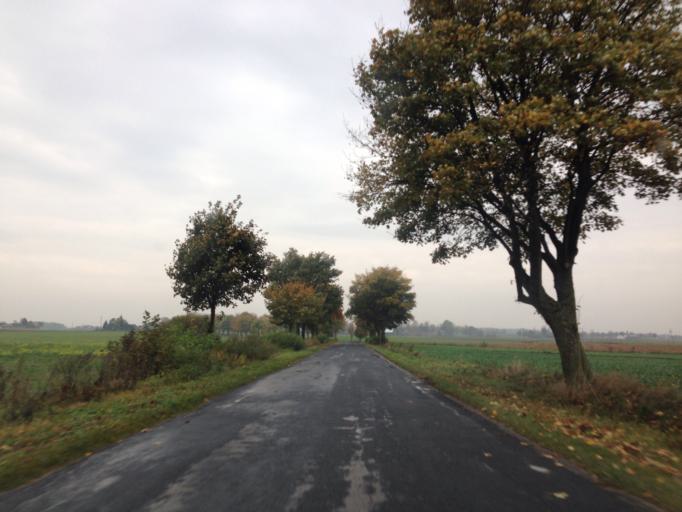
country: PL
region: Kujawsko-Pomorskie
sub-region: Powiat brodnicki
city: Swiedziebnia
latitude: 53.1504
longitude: 19.5008
